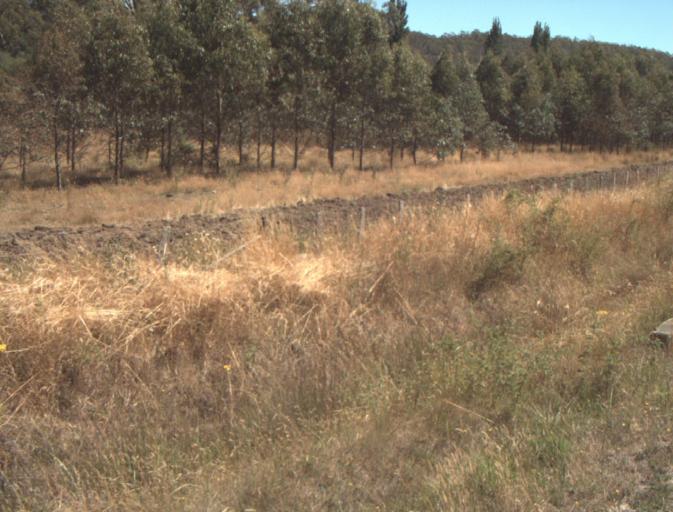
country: AU
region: Tasmania
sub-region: Launceston
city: Newstead
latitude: -41.3815
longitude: 147.3118
